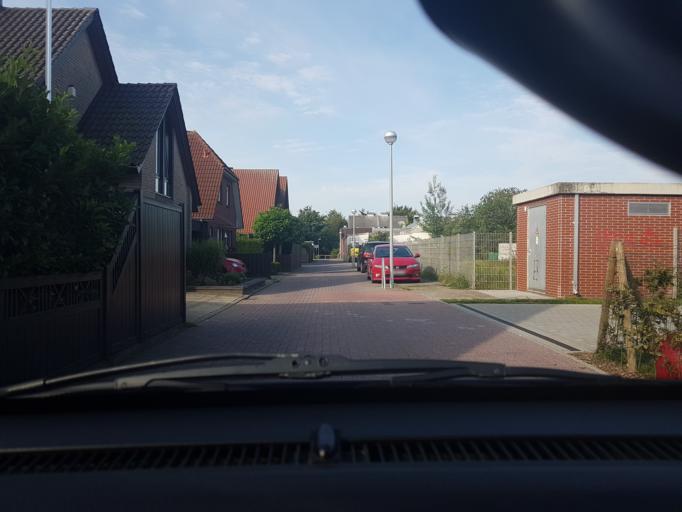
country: DE
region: North Rhine-Westphalia
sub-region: Regierungsbezirk Munster
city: Greven
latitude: 52.0976
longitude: 7.6220
